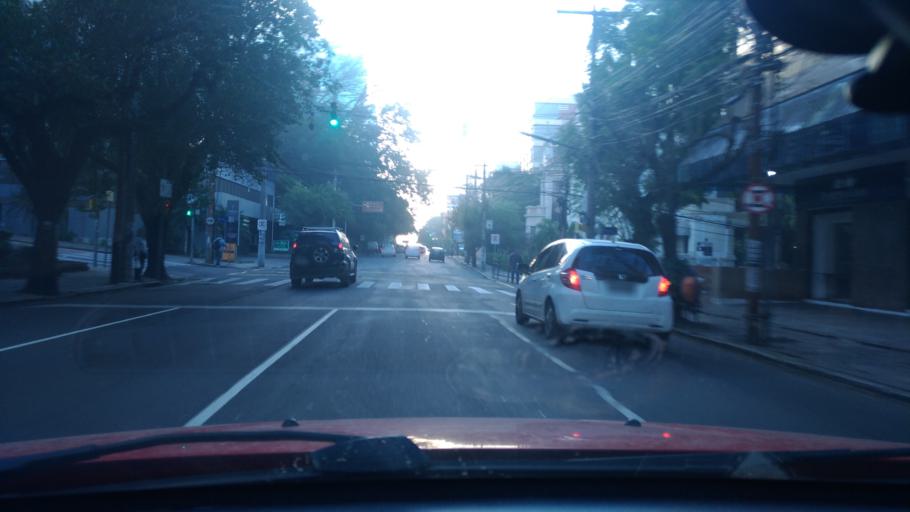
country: BR
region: Rio Grande do Sul
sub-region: Porto Alegre
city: Porto Alegre
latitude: -30.0288
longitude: -51.2062
